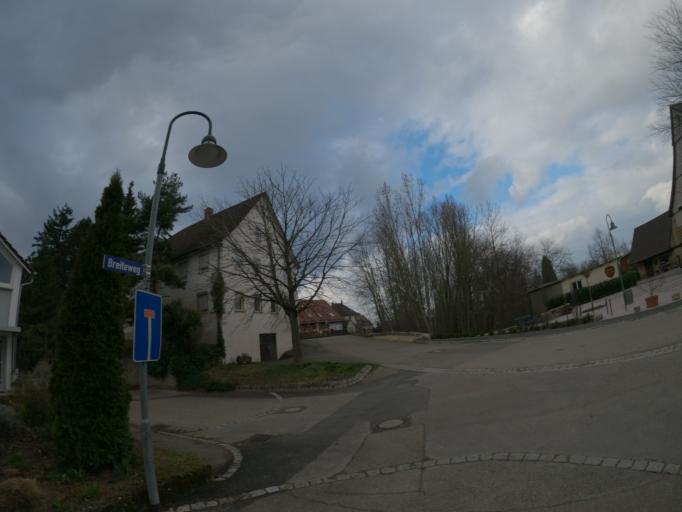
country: DE
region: Baden-Wuerttemberg
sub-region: Regierungsbezirk Stuttgart
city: Schlat
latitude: 48.6532
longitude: 9.7029
